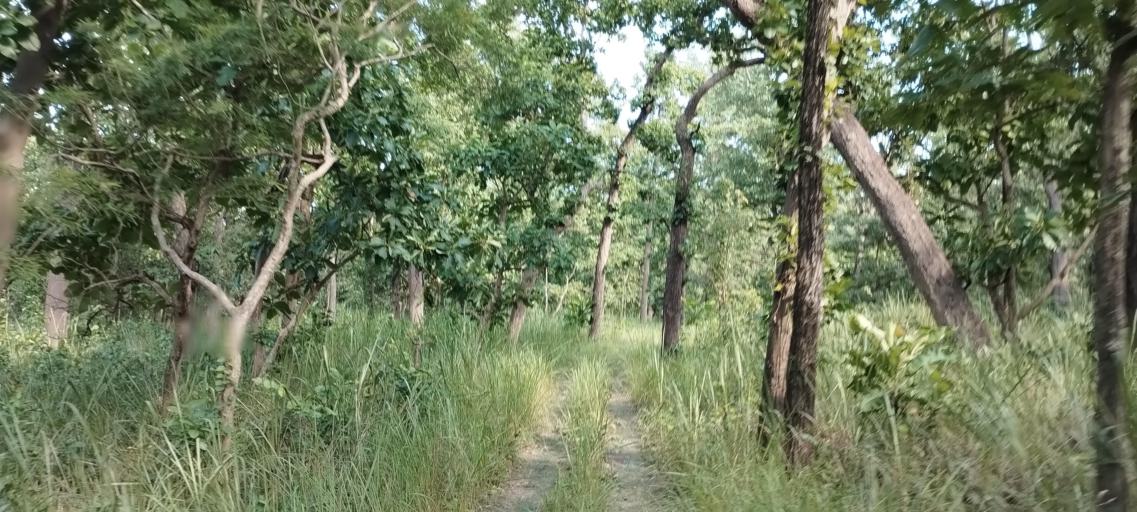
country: NP
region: Far Western
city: Tikapur
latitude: 28.5516
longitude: 81.2832
